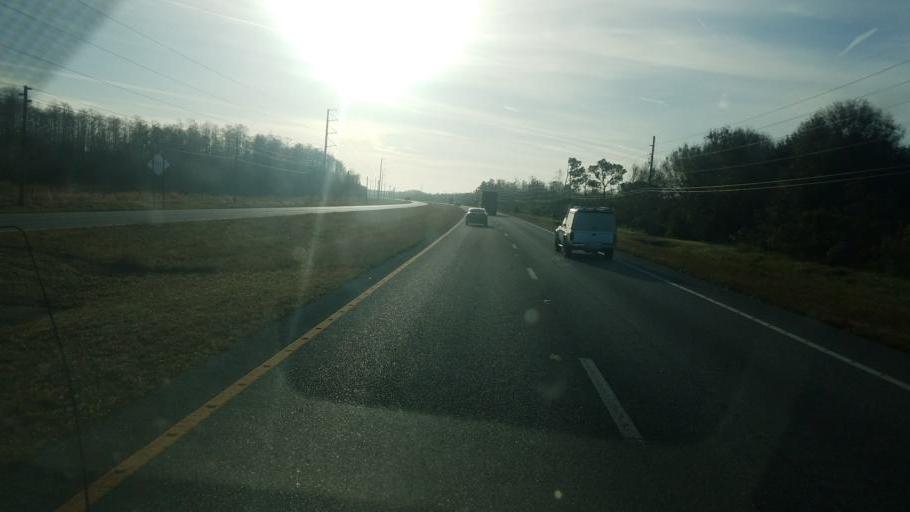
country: US
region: Florida
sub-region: Osceola County
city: Saint Cloud
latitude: 28.1524
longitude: -81.1056
